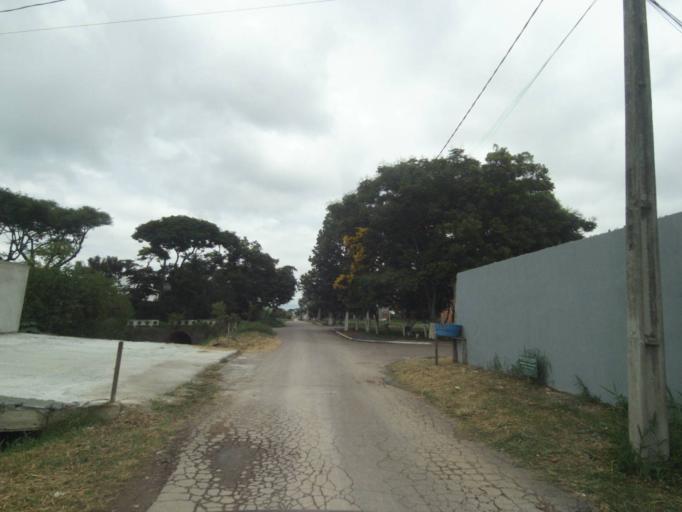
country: BR
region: Parana
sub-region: Pinhais
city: Pinhais
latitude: -25.4629
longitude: -49.1940
